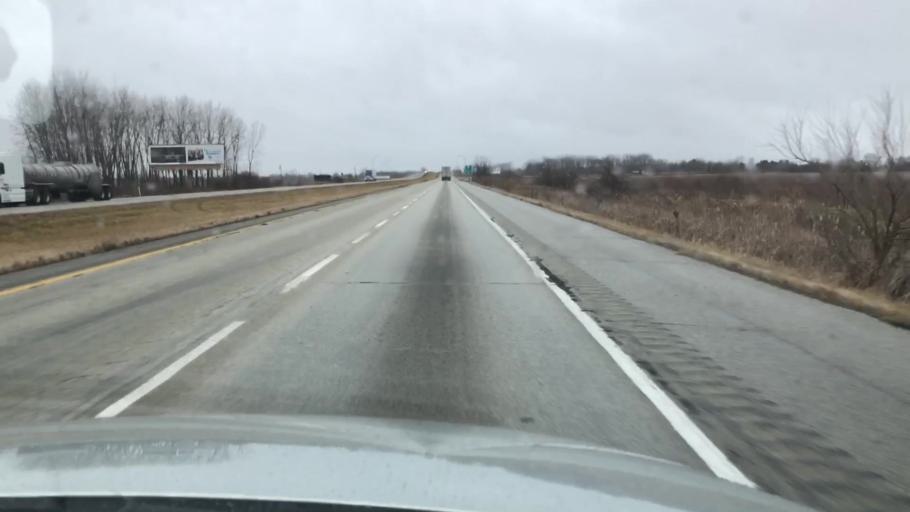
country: US
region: Indiana
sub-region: Starke County
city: Knox
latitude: 41.3940
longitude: -86.6096
